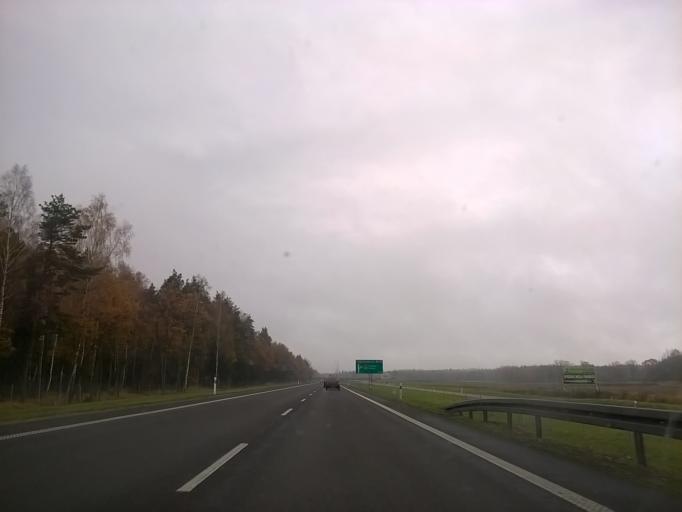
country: PL
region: Warmian-Masurian Voivodeship
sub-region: Powiat braniewski
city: Braniewo
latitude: 54.2835
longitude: 19.7830
